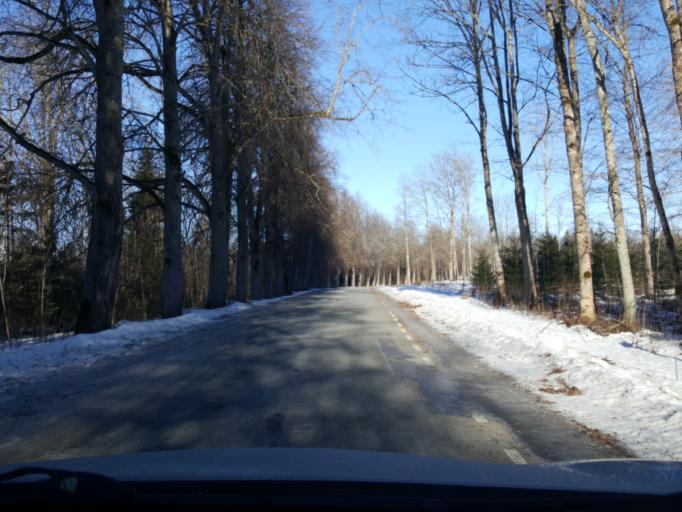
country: EE
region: Viljandimaa
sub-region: Viljandi linn
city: Viljandi
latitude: 58.4196
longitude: 25.5403
